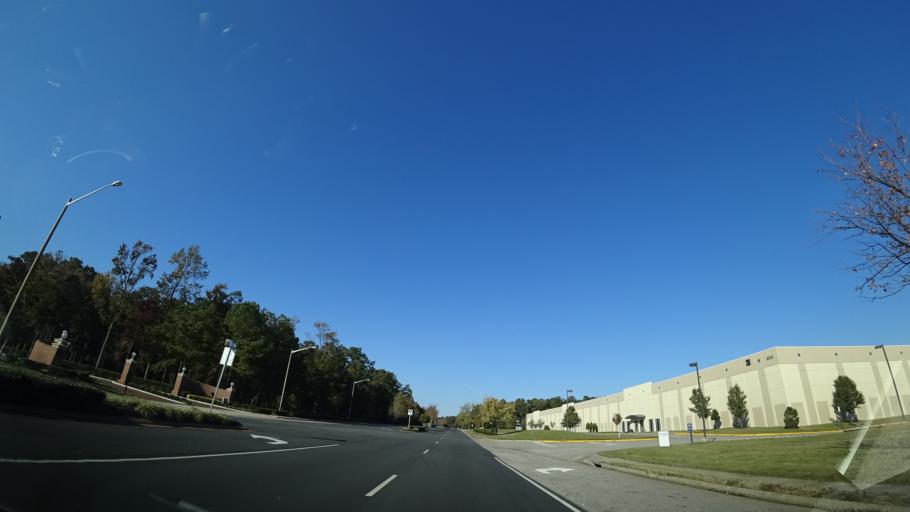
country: US
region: Virginia
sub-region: City of Newport News
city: Newport News
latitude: 36.8867
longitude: -76.4371
